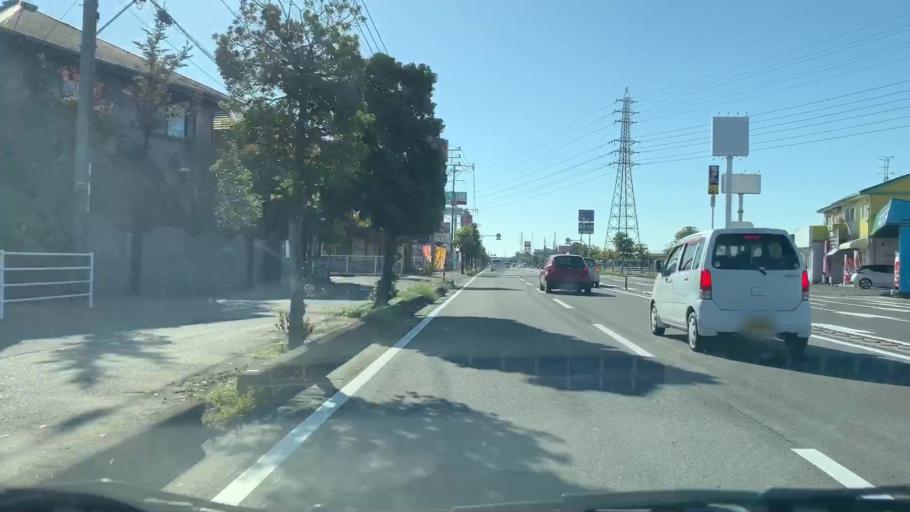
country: JP
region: Saga Prefecture
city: Saga-shi
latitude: 33.3025
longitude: 130.2795
